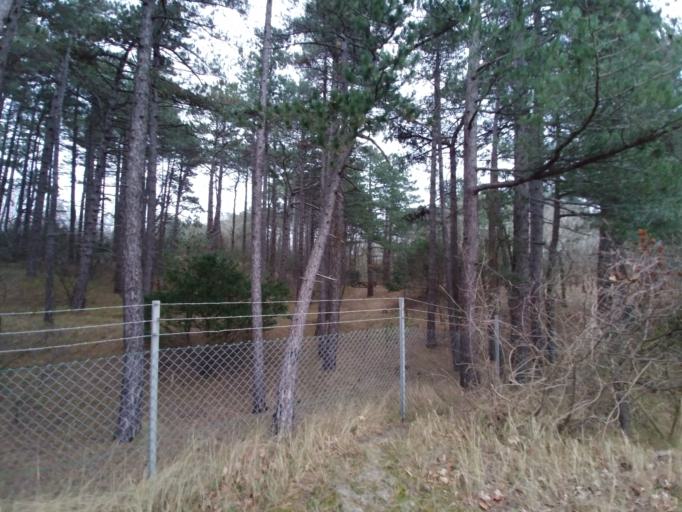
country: NL
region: South Holland
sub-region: Gemeente Leidschendam-Voorburg
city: Voorburg
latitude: 52.1258
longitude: 4.3517
